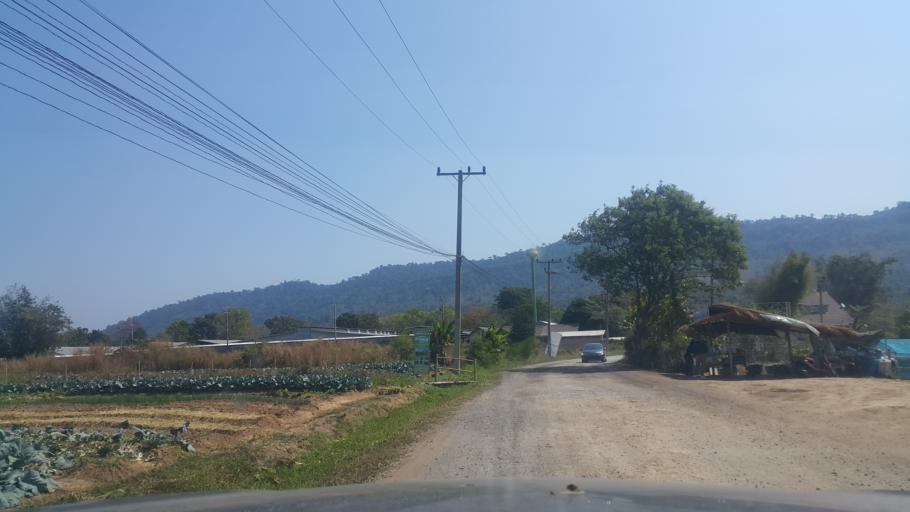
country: TH
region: Nakhon Ratchasima
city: Wang Nam Khiao
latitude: 14.3415
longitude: 101.9419
